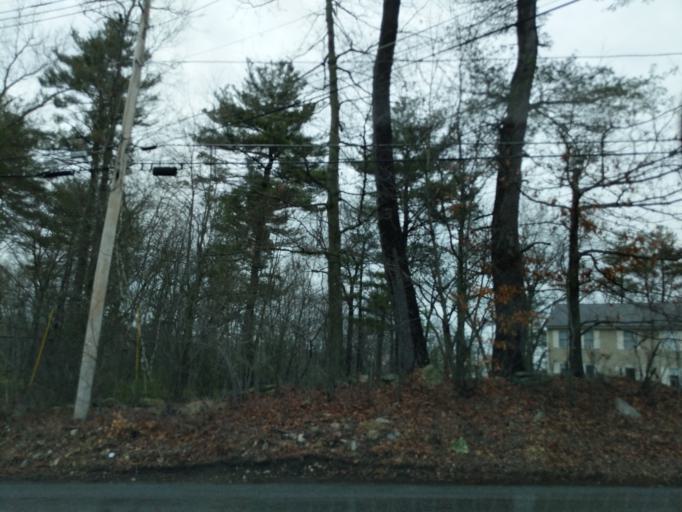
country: US
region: Massachusetts
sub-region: Worcester County
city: Whitinsville
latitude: 42.1030
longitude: -71.6867
